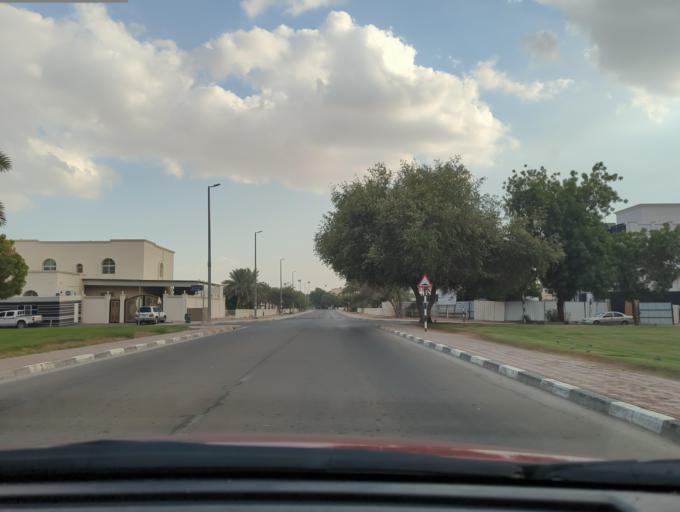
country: AE
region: Abu Dhabi
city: Al Ain
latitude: 24.1913
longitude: 55.6342
